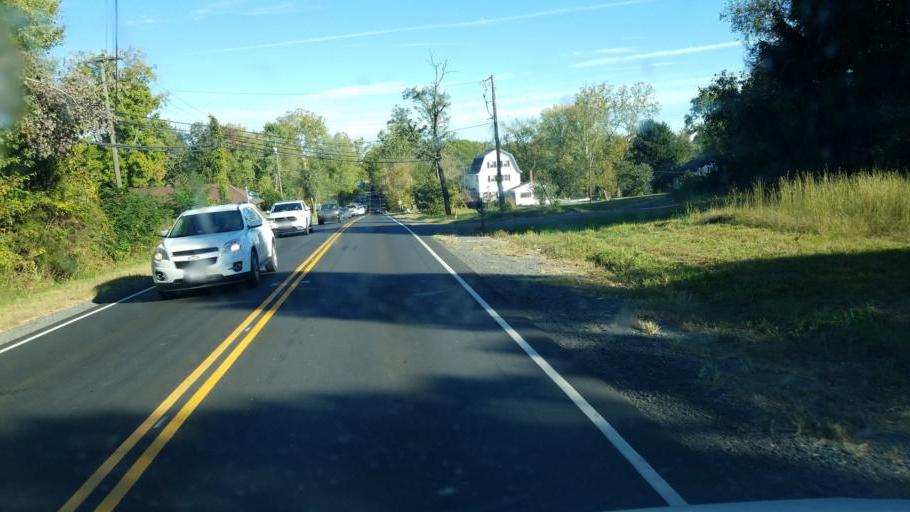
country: US
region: Virginia
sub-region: Loudoun County
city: Brambleton
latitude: 38.9526
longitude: -77.5791
